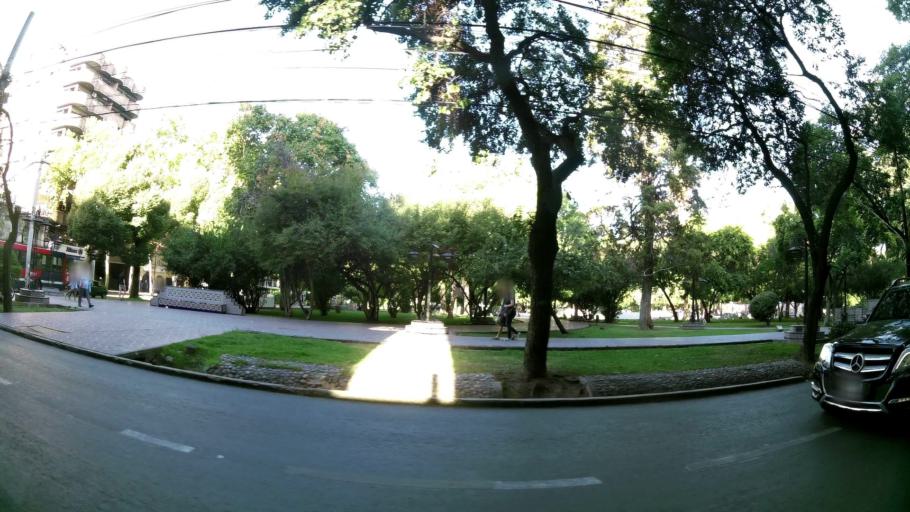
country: AR
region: Mendoza
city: Mendoza
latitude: -32.8927
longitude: -68.8424
